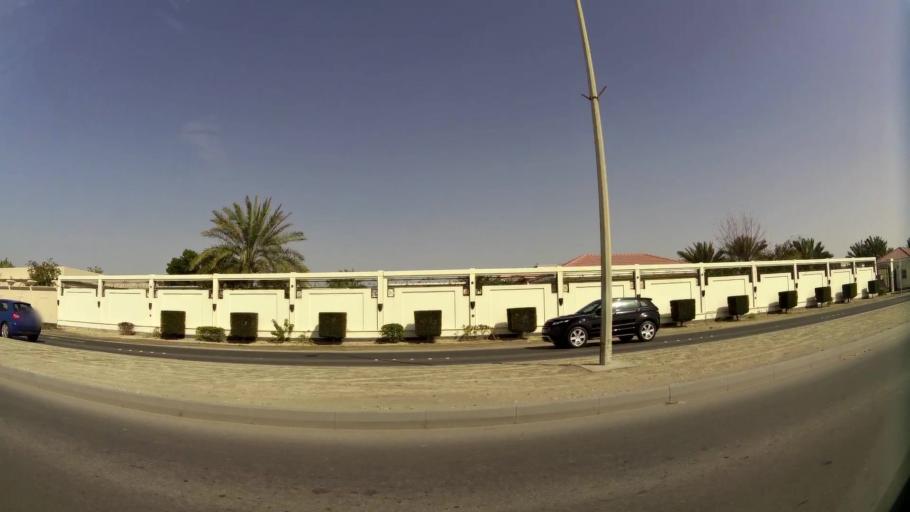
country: BH
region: Central Governorate
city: Madinat Hamad
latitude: 26.1803
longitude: 50.4656
